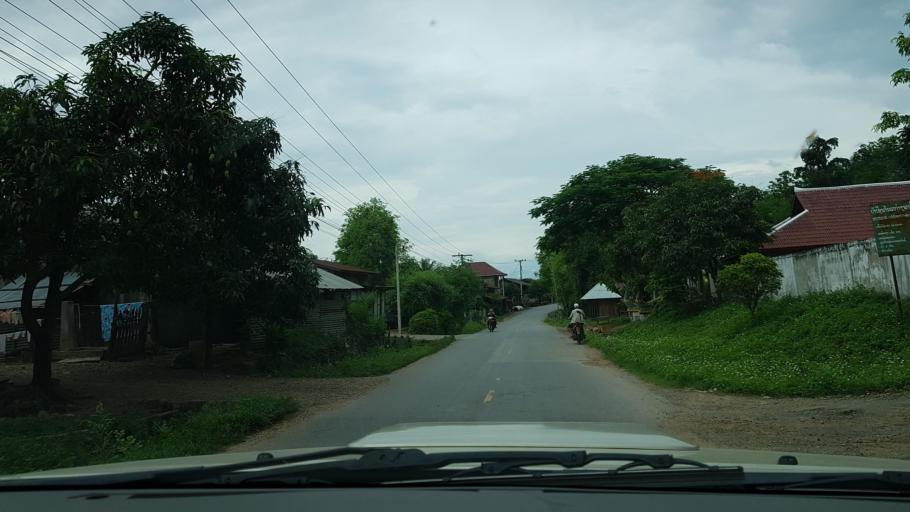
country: LA
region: Loungnamtha
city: Muang Nale
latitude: 20.3392
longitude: 101.6747
